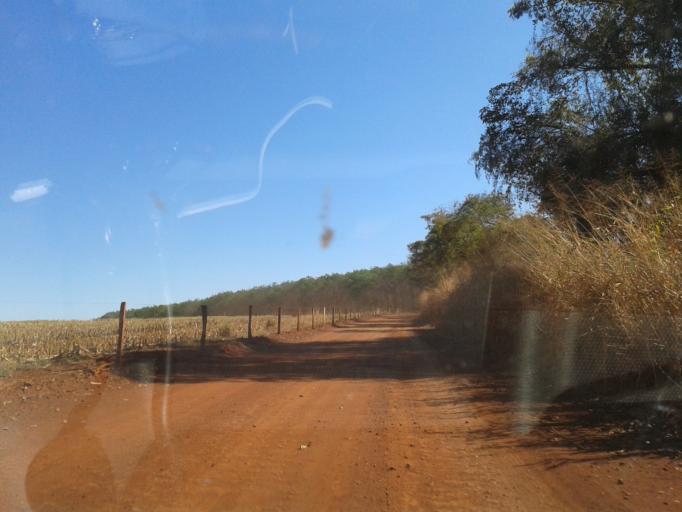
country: BR
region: Minas Gerais
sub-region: Centralina
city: Centralina
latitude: -18.5738
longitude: -49.1356
